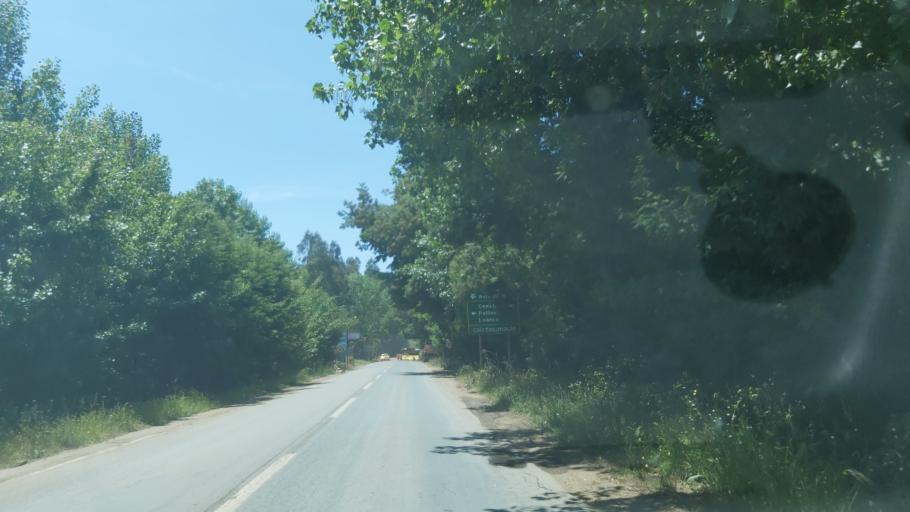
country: CL
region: Maule
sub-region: Provincia de Cauquenes
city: Cauquenes
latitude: -35.7942
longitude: -72.5432
